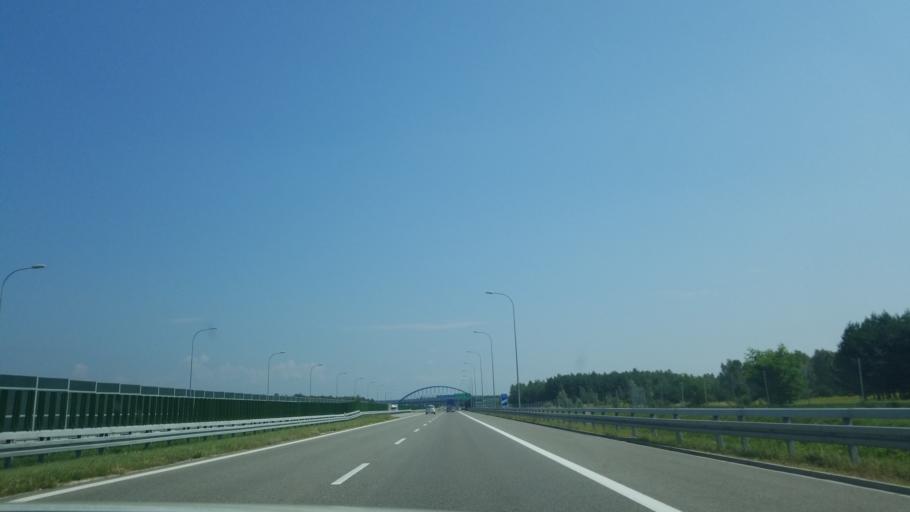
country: PL
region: Subcarpathian Voivodeship
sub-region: Powiat ropczycko-sedziszowski
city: Sedziszow Malopolski
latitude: 50.1090
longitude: 21.6561
